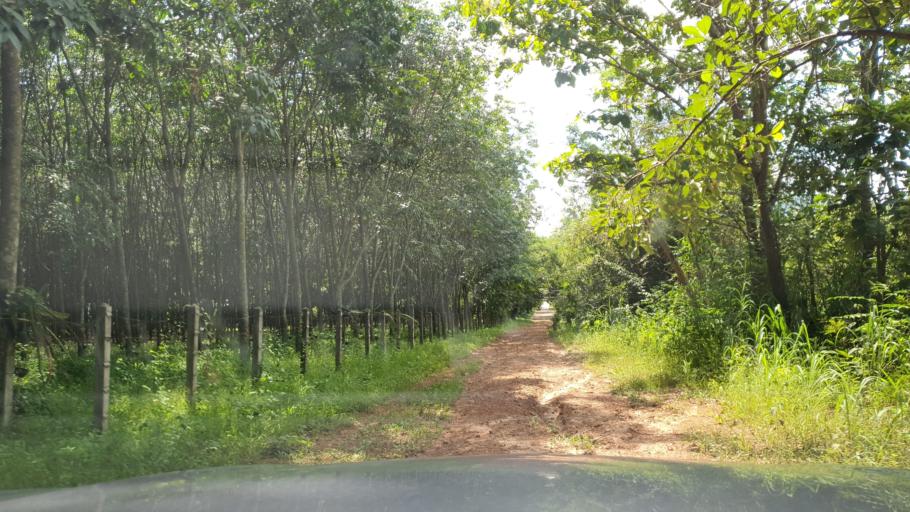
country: TH
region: Chiang Mai
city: Mae On
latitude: 18.7354
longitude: 99.2389
